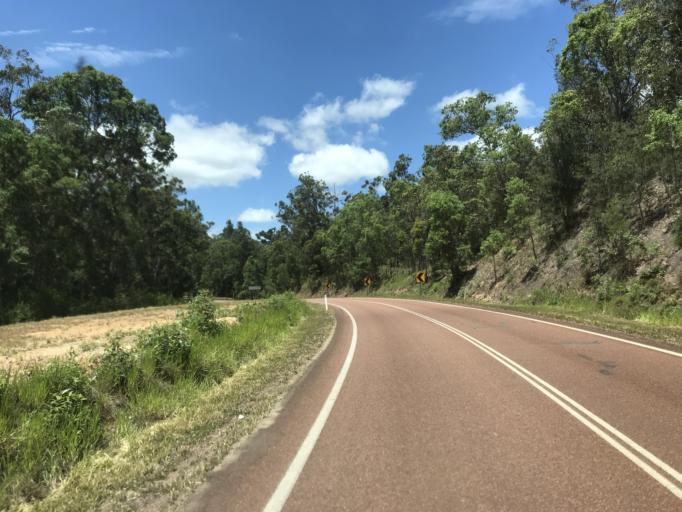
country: AU
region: Queensland
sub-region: Tablelands
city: Ravenshoe
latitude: -17.5968
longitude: 145.4782
